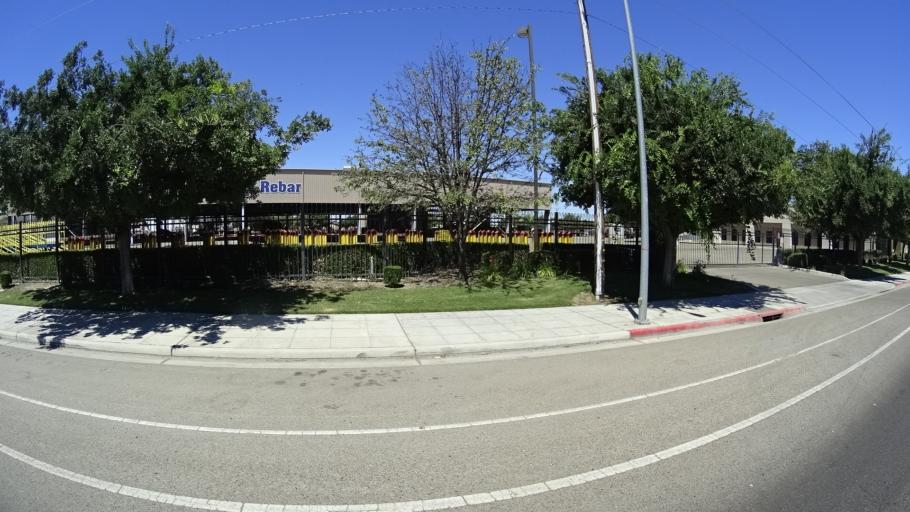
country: US
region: California
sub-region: Fresno County
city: Fresno
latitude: 36.6987
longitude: -119.7727
